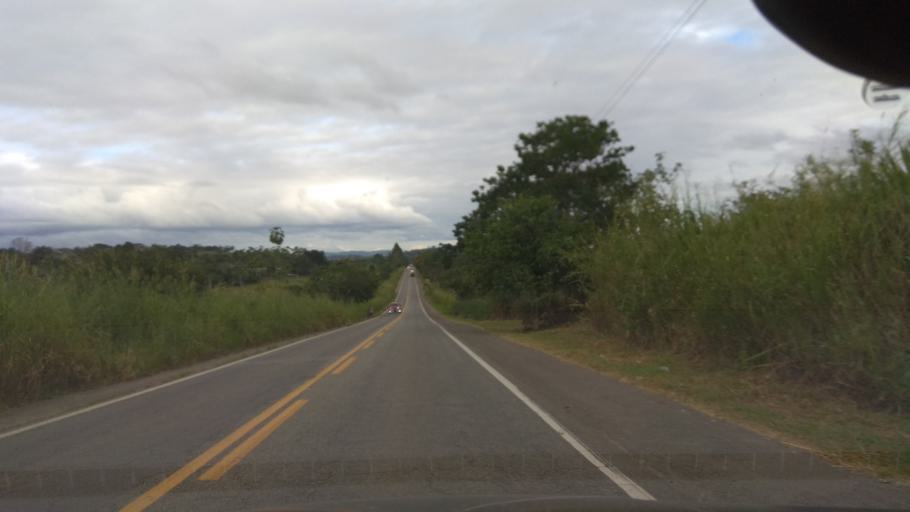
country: BR
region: Bahia
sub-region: Ipiau
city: Ipiau
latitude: -14.1559
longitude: -39.6960
